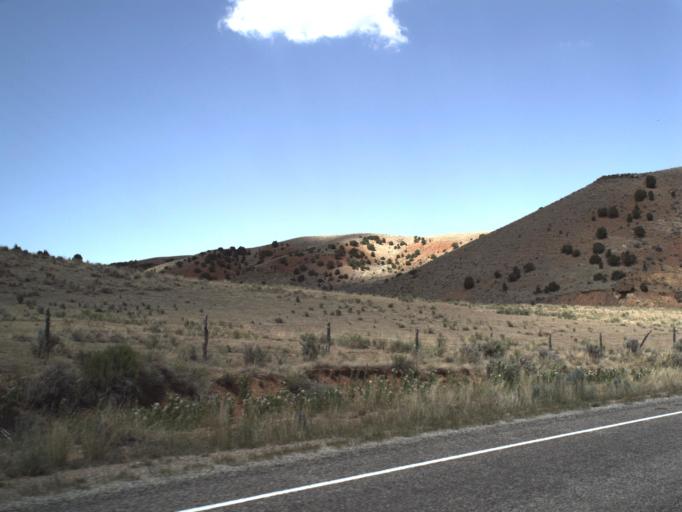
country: US
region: Utah
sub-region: Rich County
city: Randolph
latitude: 41.5063
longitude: -111.2372
